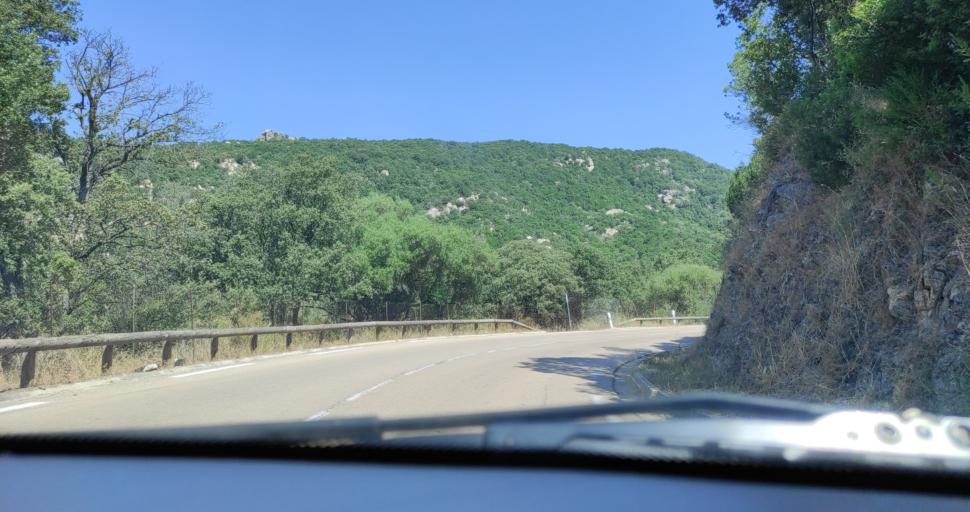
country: FR
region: Corsica
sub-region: Departement de la Corse-du-Sud
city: Sartene
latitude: 41.6090
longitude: 8.9437
